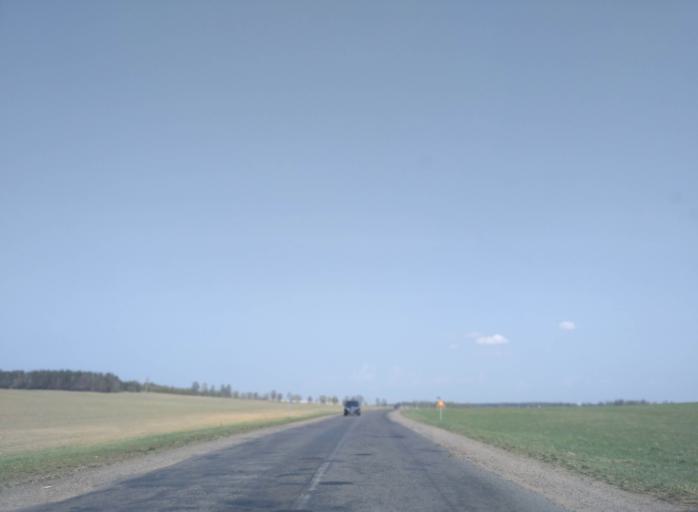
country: BY
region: Minsk
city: Horad Barysaw
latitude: 54.3191
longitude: 28.5620
